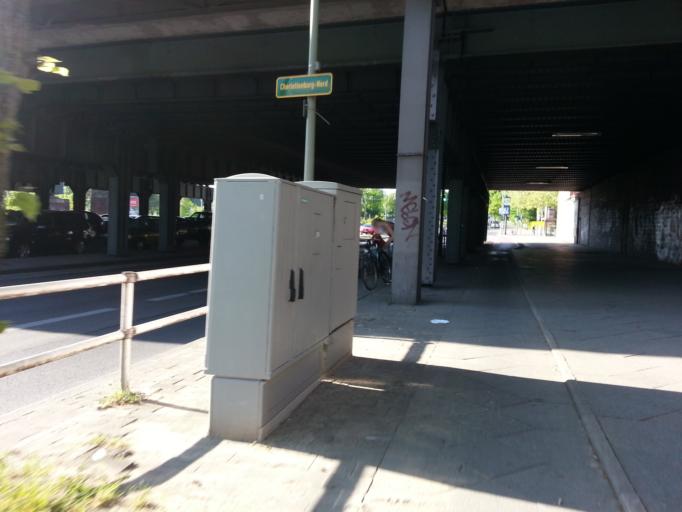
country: DE
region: Berlin
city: Charlottenburg-Nord
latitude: 52.5296
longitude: 13.2965
